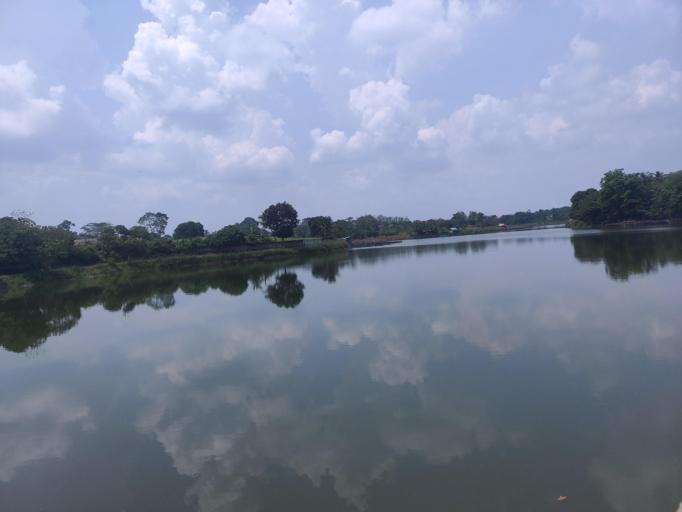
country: ID
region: West Java
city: Parung
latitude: -6.4699
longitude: 106.7138
